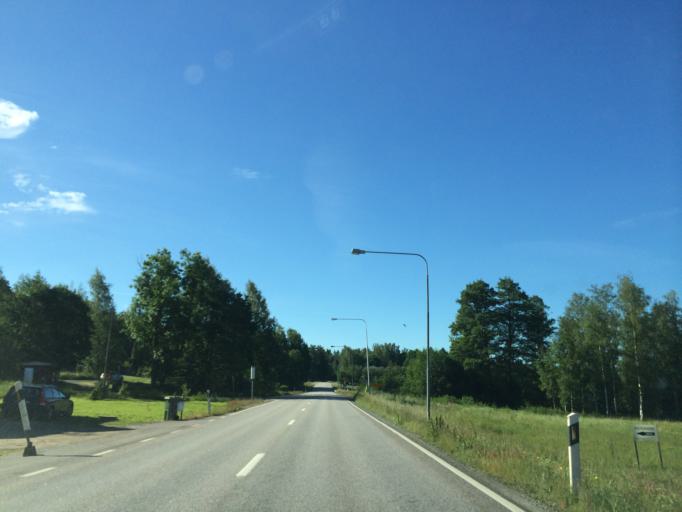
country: SE
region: OEstergoetland
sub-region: Motala Kommun
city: Ryd
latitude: 58.7358
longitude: 14.9837
